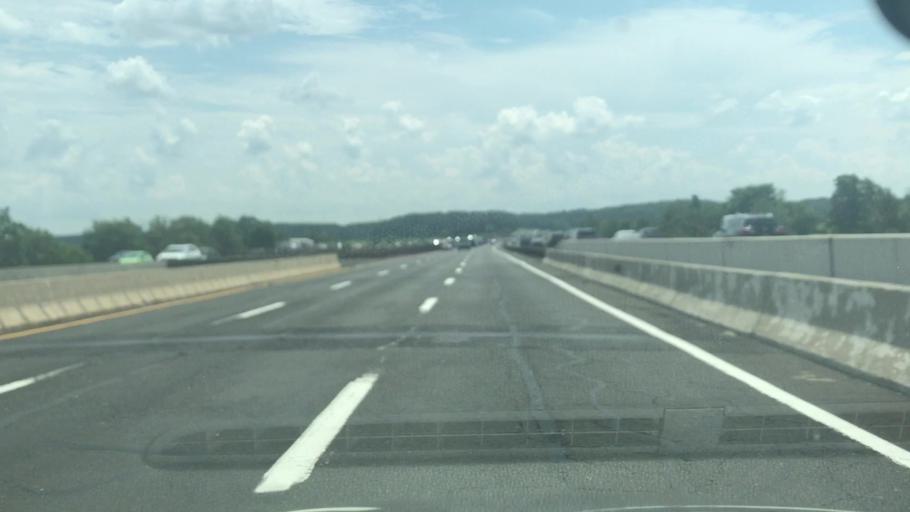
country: US
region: New Jersey
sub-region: Middlesex County
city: Laurence Harbor
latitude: 40.4541
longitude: -74.2735
